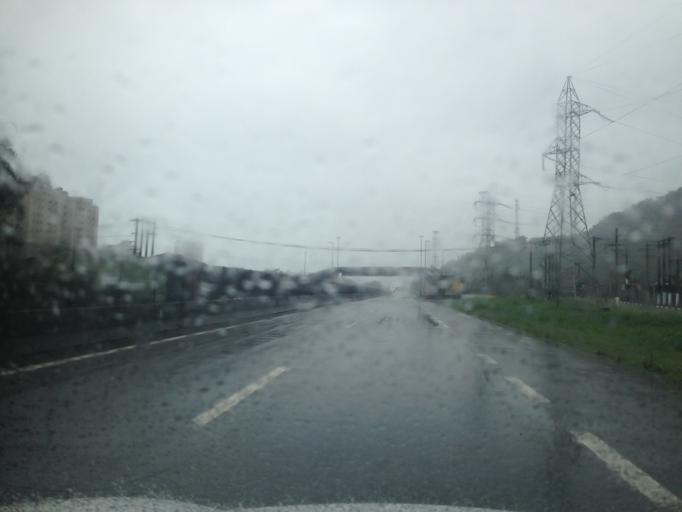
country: BR
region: Sao Paulo
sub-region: Mongagua
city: Mongagua
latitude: -24.0960
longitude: -46.6276
